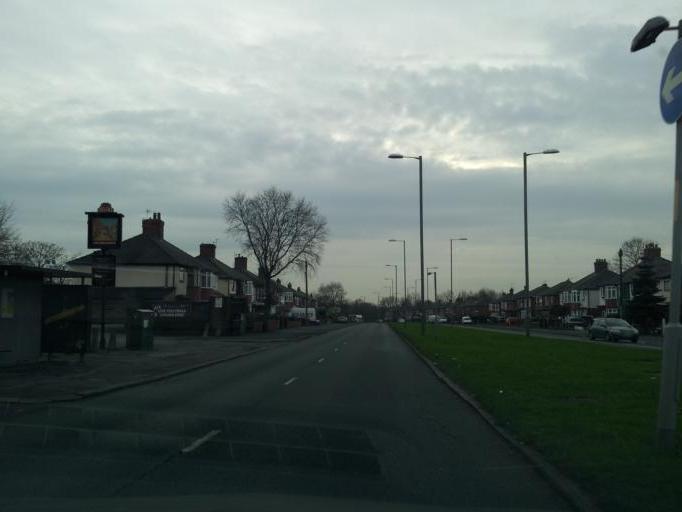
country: GB
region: England
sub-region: Manchester
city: Failsworth
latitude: 53.5167
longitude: -2.1689
